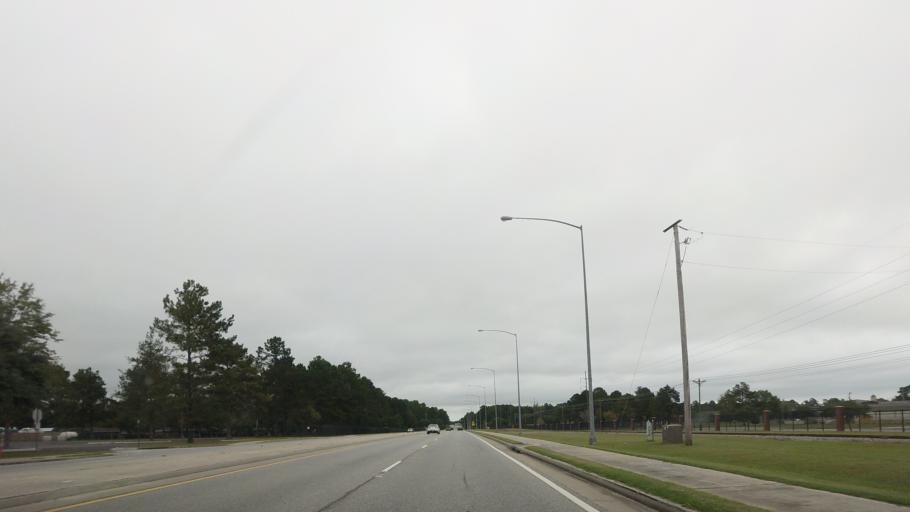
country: US
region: Georgia
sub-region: Berrien County
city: Ray City
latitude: 30.9752
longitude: -83.2120
